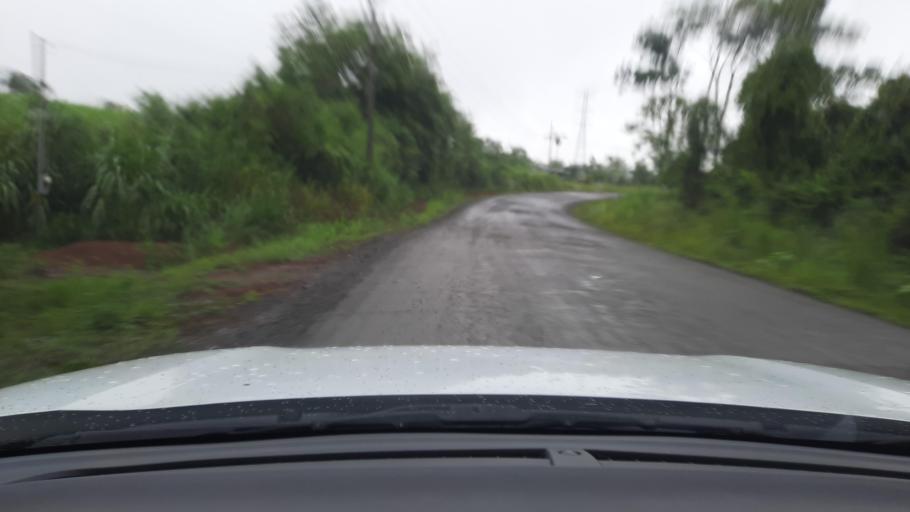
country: NI
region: Rivas
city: Cardenas
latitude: 11.0311
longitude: -85.3666
